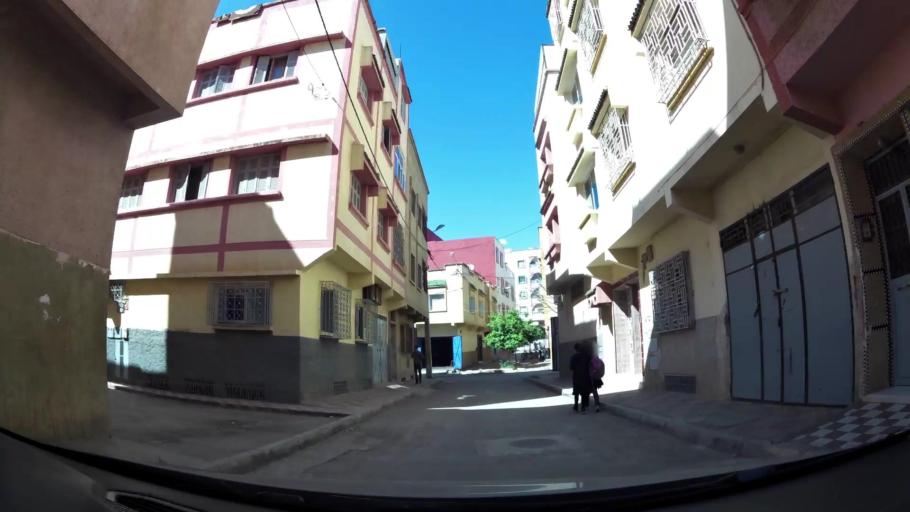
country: MA
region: Meknes-Tafilalet
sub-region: Meknes
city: Meknes
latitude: 33.8864
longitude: -5.5771
